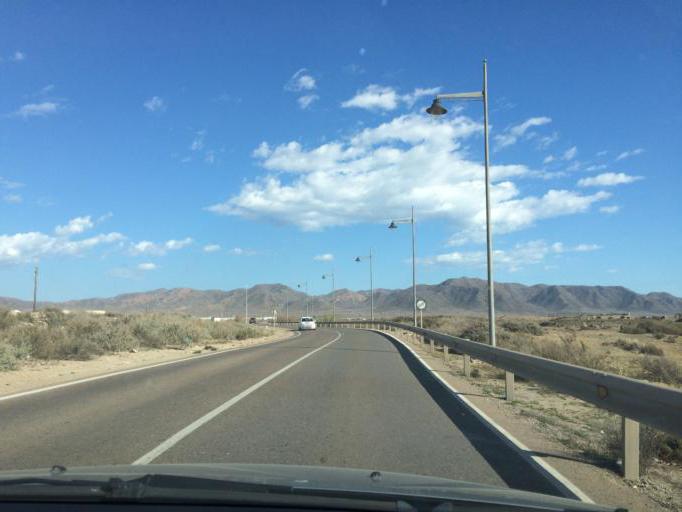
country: ES
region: Andalusia
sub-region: Provincia de Almeria
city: Retamar
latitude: 36.7805
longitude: -2.2376
